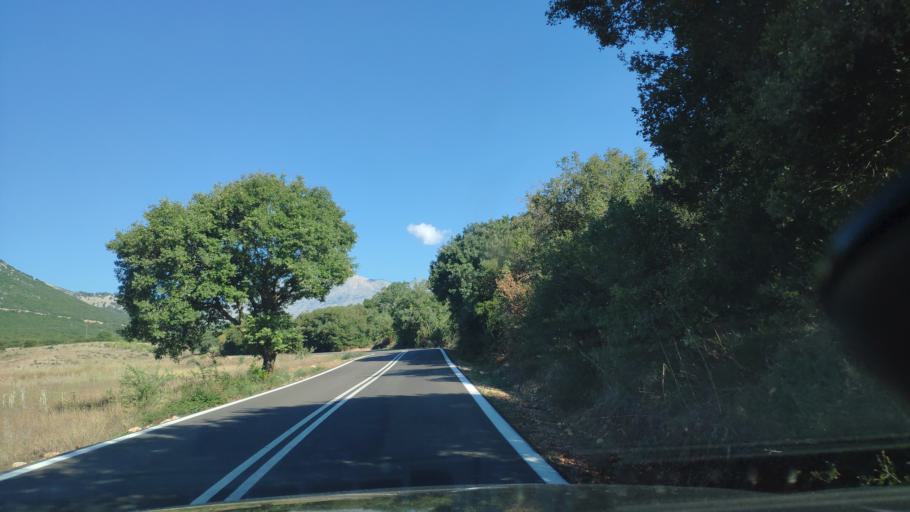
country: GR
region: West Greece
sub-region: Nomos Aitolias kai Akarnanias
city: Fitiai
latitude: 38.6803
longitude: 21.1327
